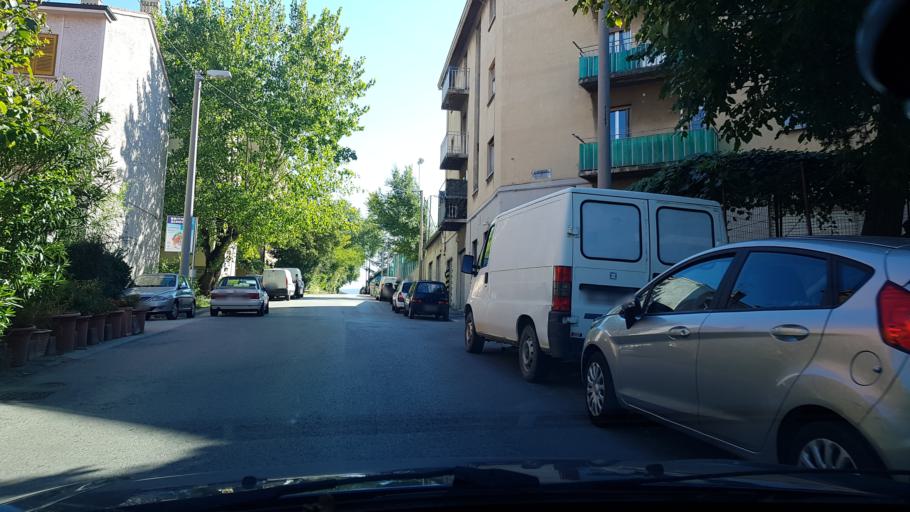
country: IT
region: Friuli Venezia Giulia
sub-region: Provincia di Trieste
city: Trieste
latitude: 45.6219
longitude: 13.7951
